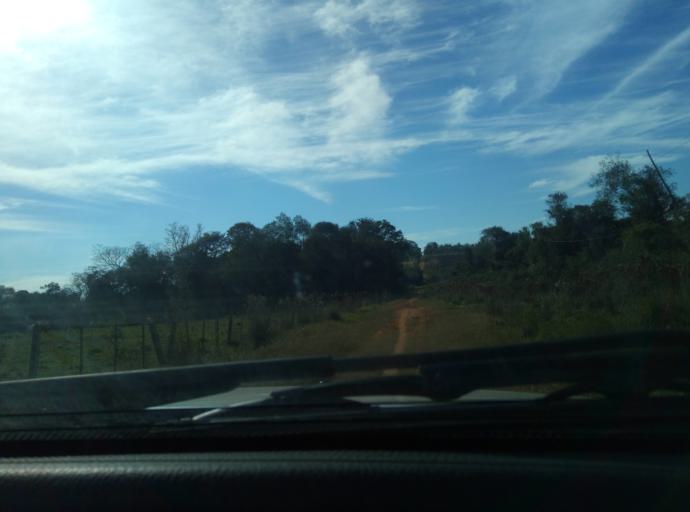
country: PY
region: Caaguazu
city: Carayao
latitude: -25.1674
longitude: -56.2929
